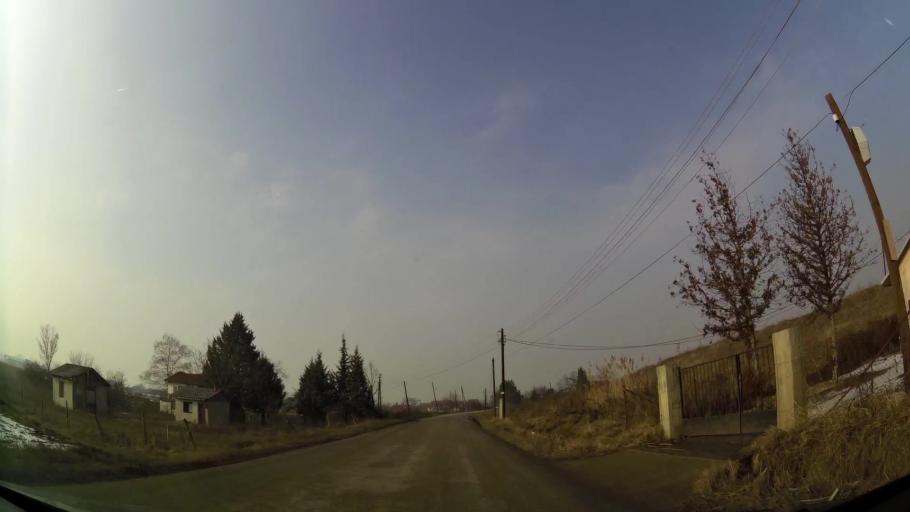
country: MK
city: Kadino
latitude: 41.9788
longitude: 21.5989
